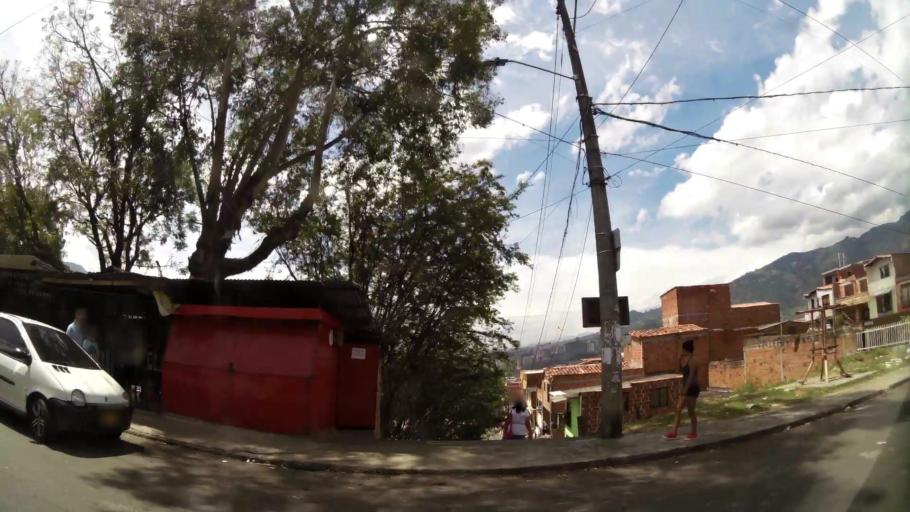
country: CO
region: Antioquia
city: Bello
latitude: 6.3477
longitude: -75.5537
